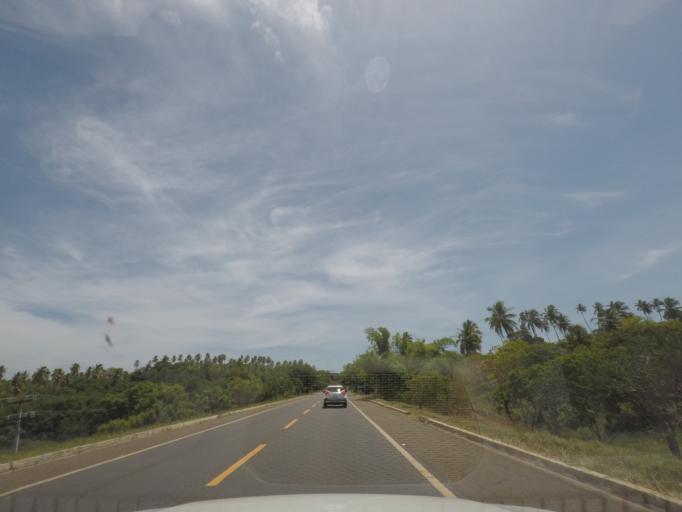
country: BR
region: Bahia
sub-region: Mata De Sao Joao
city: Mata de Sao Joao
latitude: -12.4459
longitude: -37.9512
